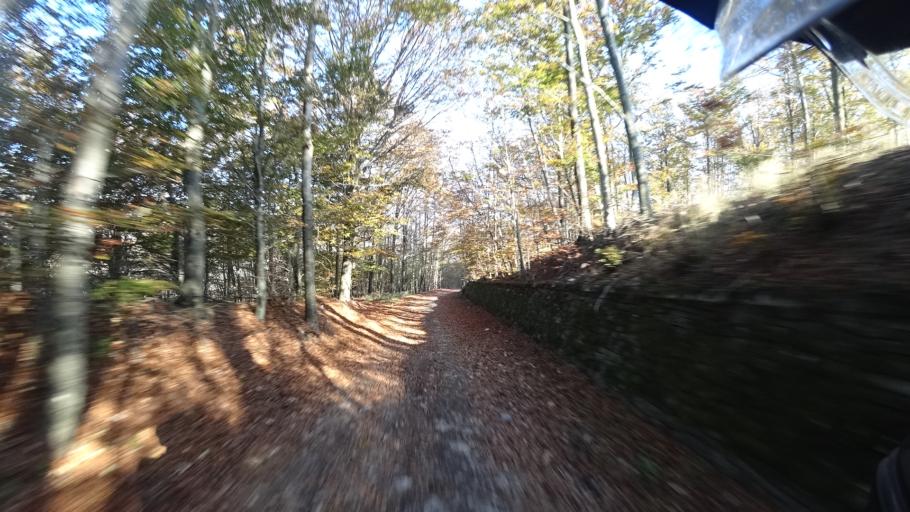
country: HR
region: Primorsko-Goranska
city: Klana
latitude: 45.4847
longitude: 14.3680
